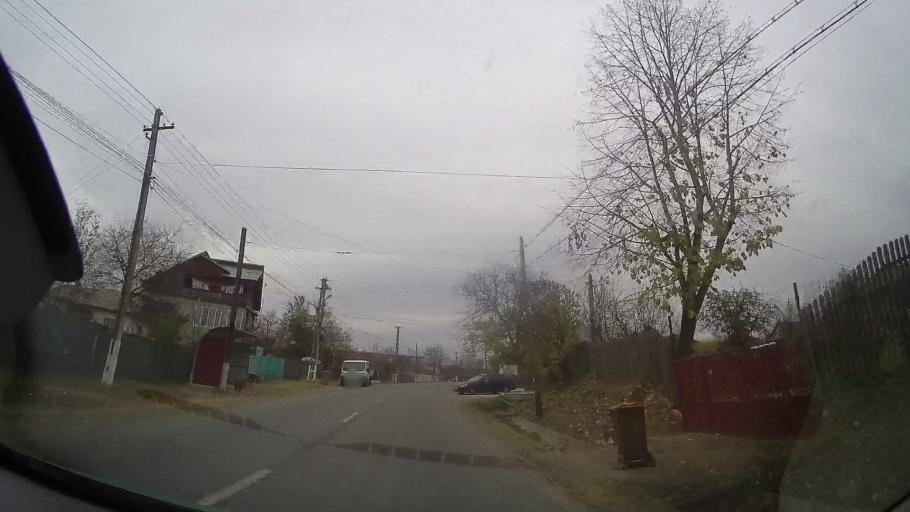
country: RO
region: Prahova
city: Mocesti
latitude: 45.0599
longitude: 26.2437
